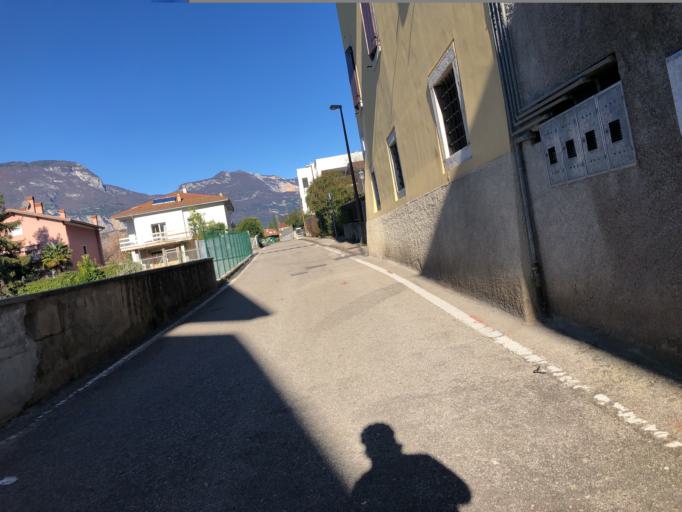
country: IT
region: Trentino-Alto Adige
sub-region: Provincia di Trento
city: Bolognano-Vignole
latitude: 45.9094
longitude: 10.9032
